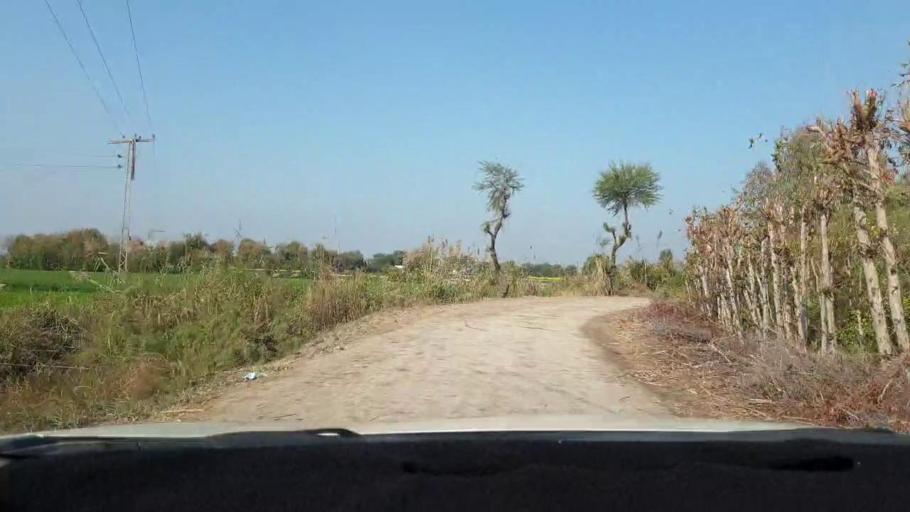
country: PK
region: Sindh
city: Berani
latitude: 25.8019
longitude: 68.8363
